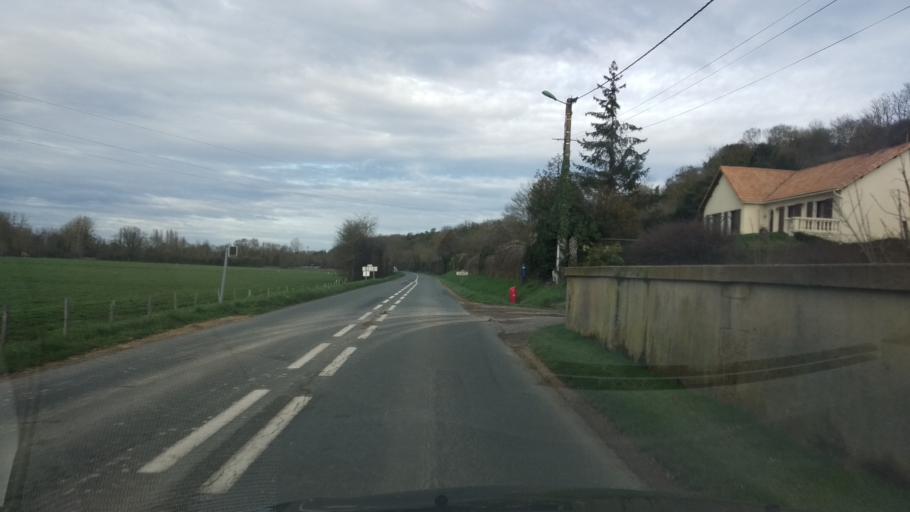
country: FR
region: Poitou-Charentes
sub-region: Departement de la Vienne
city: Chasseneuil-du-Poitou
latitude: 46.6373
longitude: 0.3751
